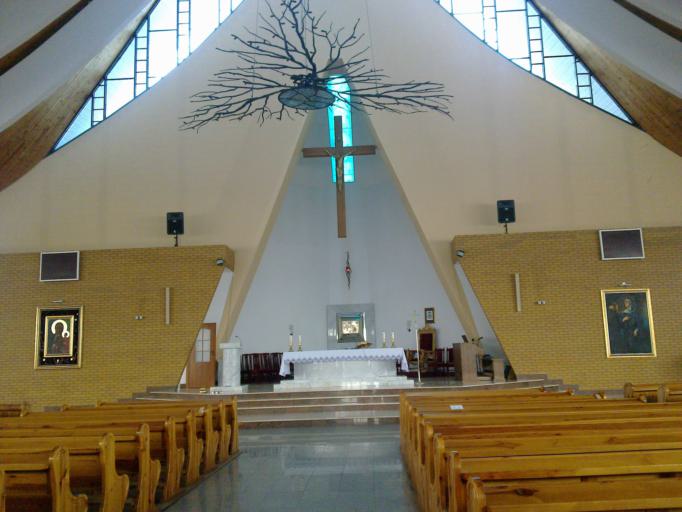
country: PL
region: Pomeranian Voivodeship
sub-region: Powiat gdanski
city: Kowale
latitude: 54.3407
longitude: 18.5599
